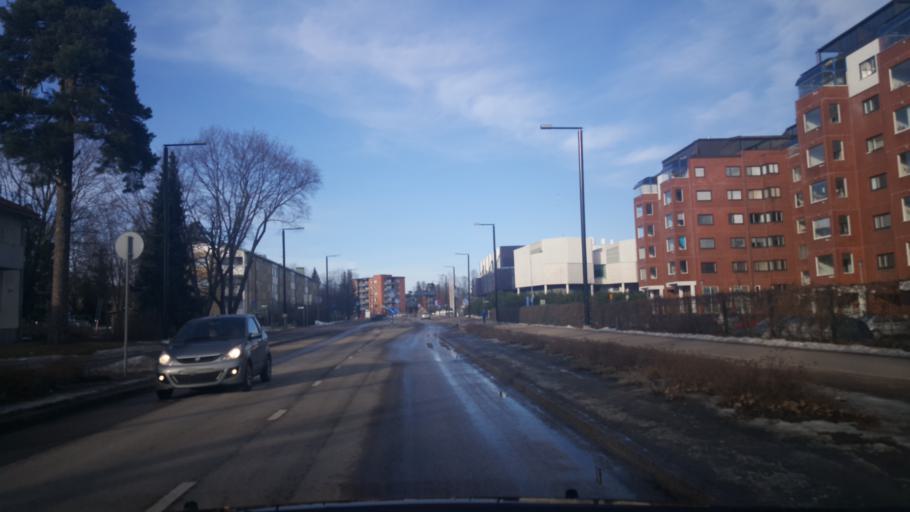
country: FI
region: Uusimaa
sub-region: Helsinki
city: Vantaa
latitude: 60.2971
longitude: 25.0399
